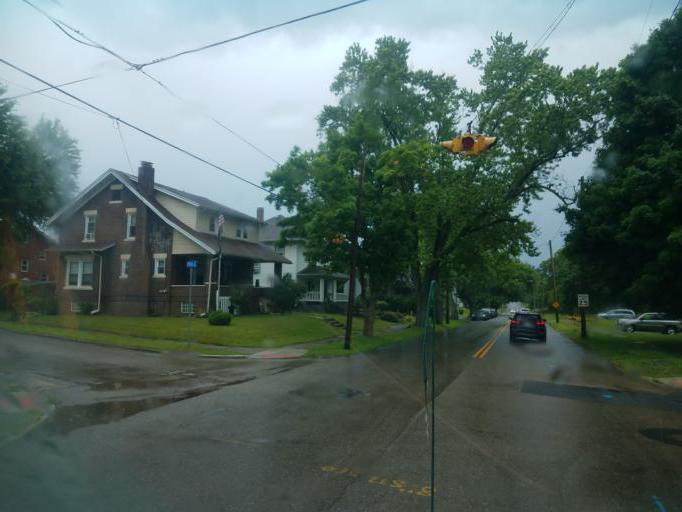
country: US
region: Ohio
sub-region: Stark County
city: Massillon
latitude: 40.7908
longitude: -81.5420
